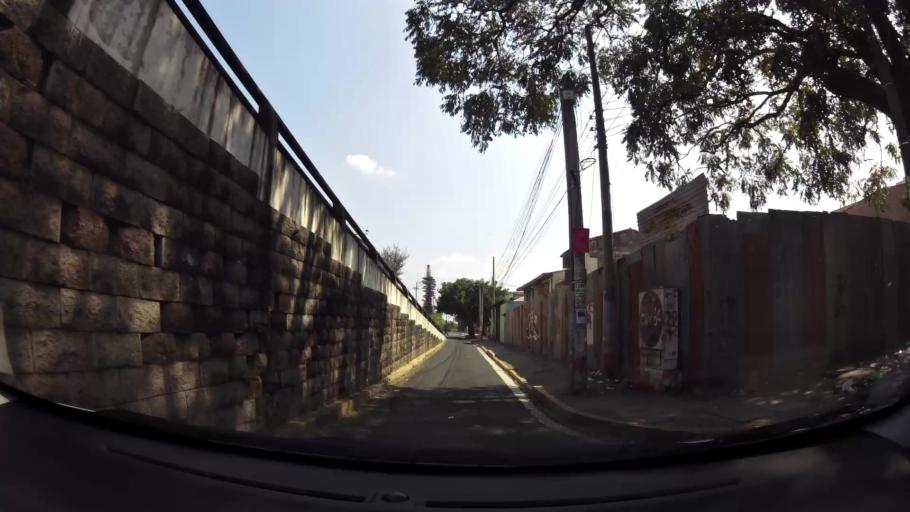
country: SV
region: San Salvador
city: San Salvador
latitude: 13.7024
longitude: -89.2150
